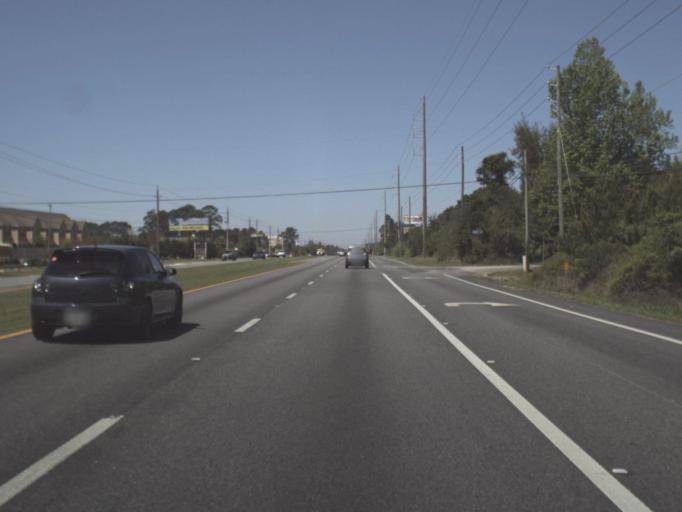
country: US
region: Florida
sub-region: Okaloosa County
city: Mary Esther
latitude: 30.4115
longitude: -86.7527
